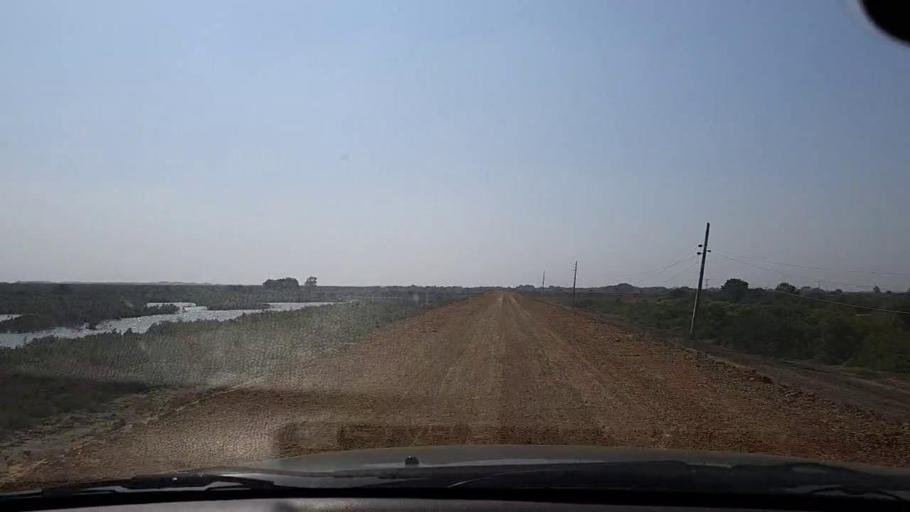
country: PK
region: Sindh
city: Chuhar Jamali
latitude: 24.4577
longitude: 67.8773
